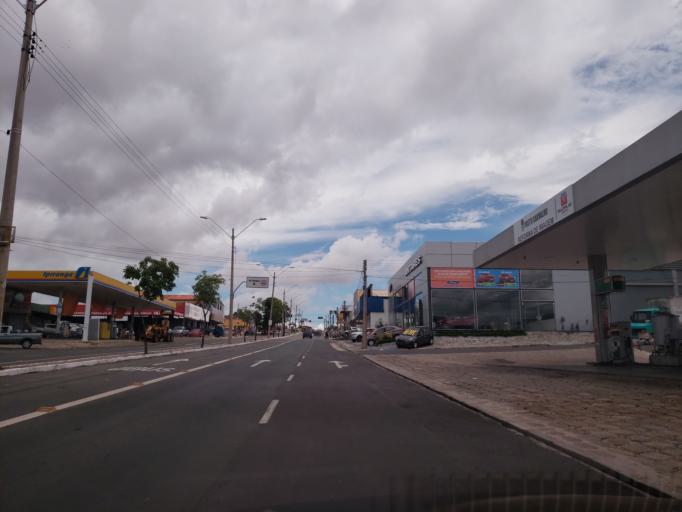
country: BR
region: Piaui
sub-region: Teresina
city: Teresina
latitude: -5.1117
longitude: -42.8066
